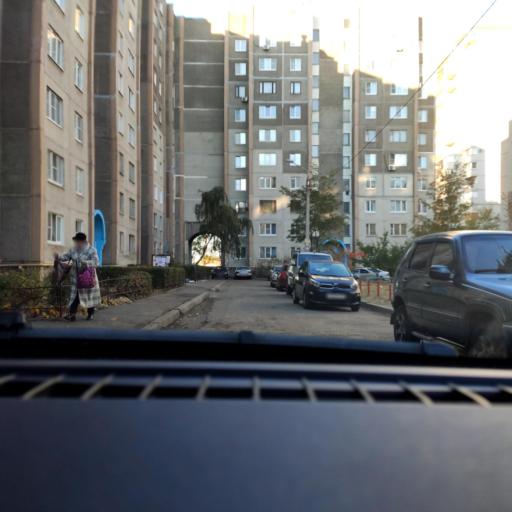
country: RU
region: Voronezj
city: Maslovka
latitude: 51.5941
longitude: 39.2423
